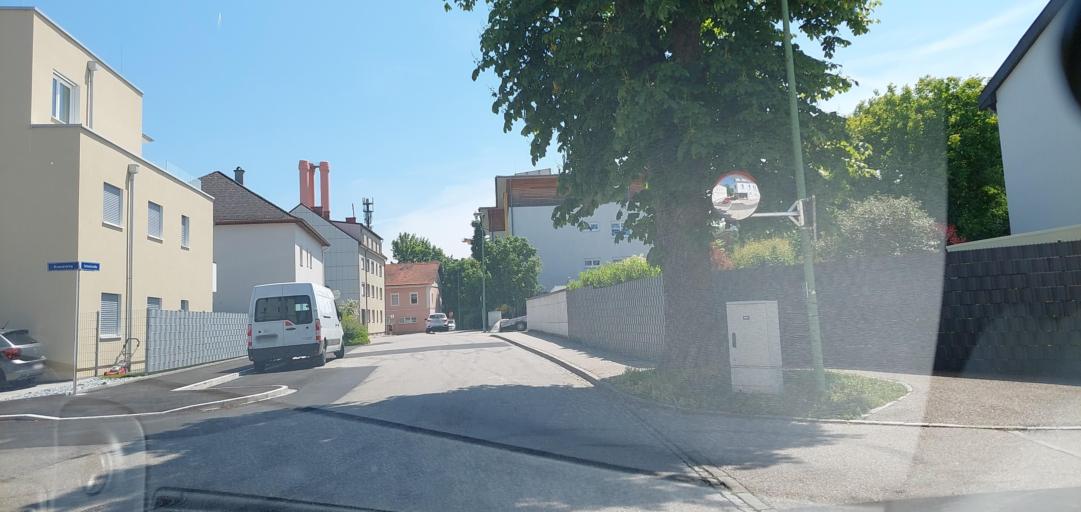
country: AT
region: Upper Austria
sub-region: Wels-Land
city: Thalheim bei Wels
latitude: 48.1534
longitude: 14.0056
